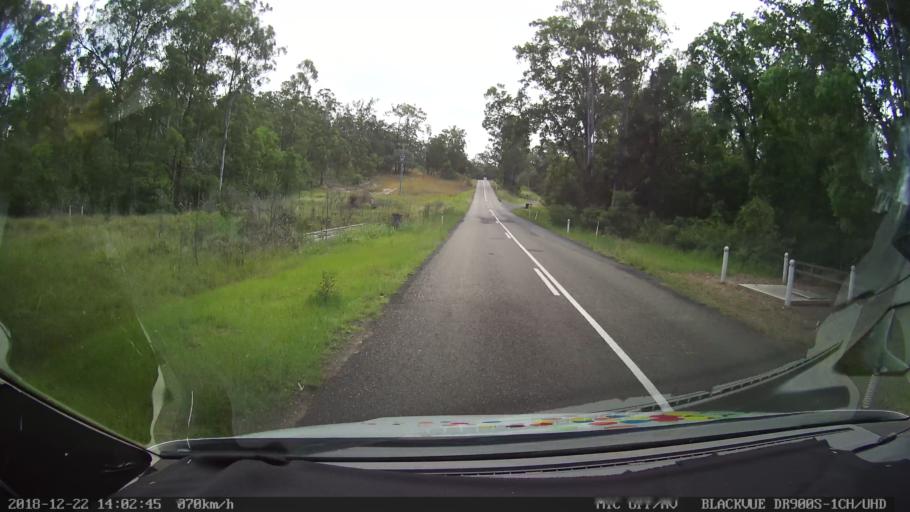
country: AU
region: New South Wales
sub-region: Clarence Valley
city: Coutts Crossing
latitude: -29.9262
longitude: 152.7464
